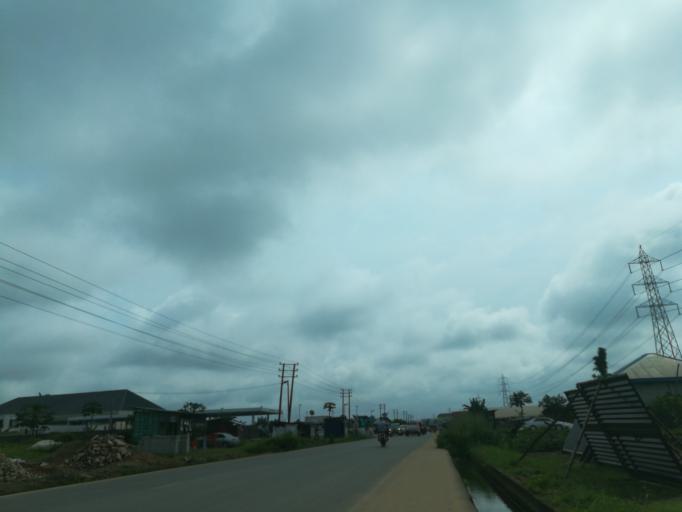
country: NG
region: Rivers
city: Emuoha
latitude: 4.8930
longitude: 6.9752
